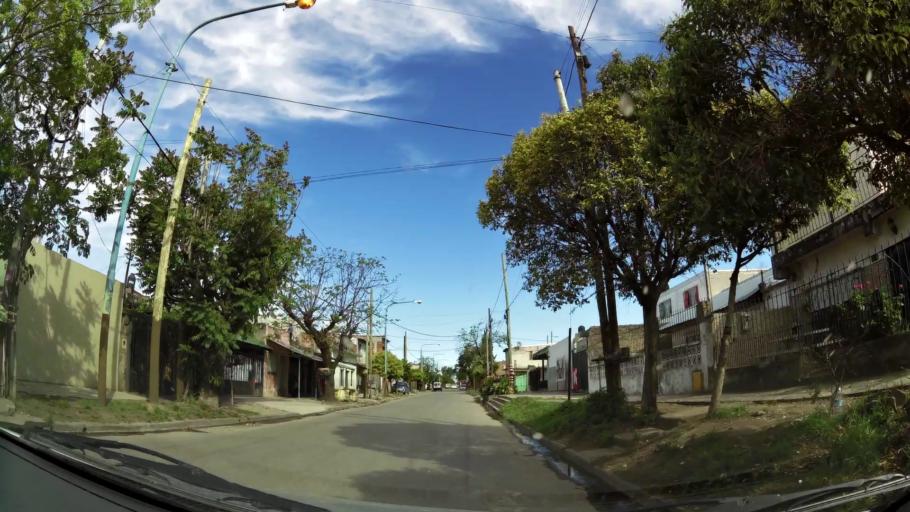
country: AR
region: Buenos Aires
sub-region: Partido de Quilmes
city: Quilmes
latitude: -34.7684
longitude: -58.3077
